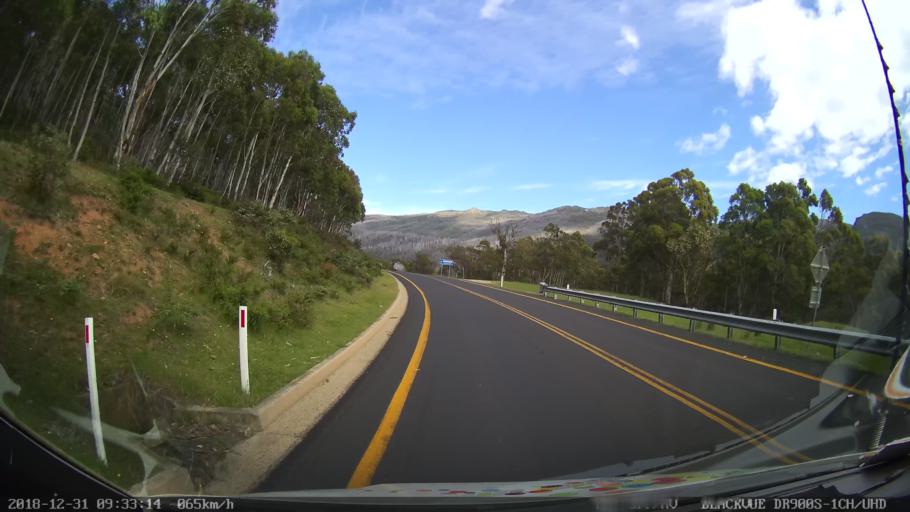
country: AU
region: New South Wales
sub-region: Snowy River
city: Jindabyne
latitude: -36.4510
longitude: 148.4249
